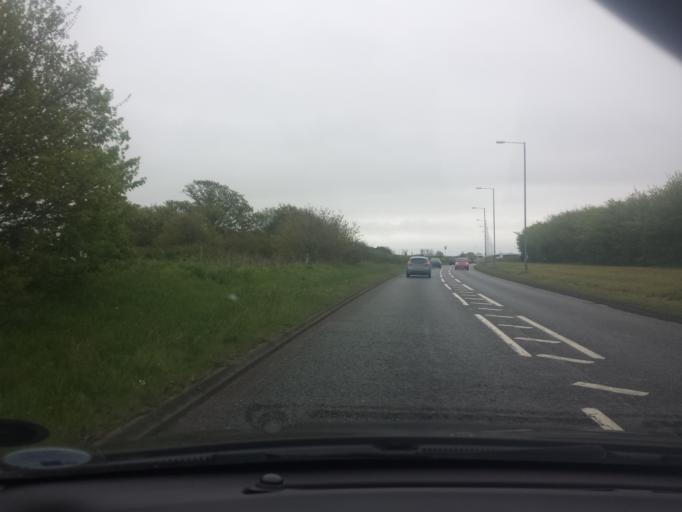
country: GB
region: England
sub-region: Essex
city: Little Clacton
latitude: 51.8198
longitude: 1.1557
